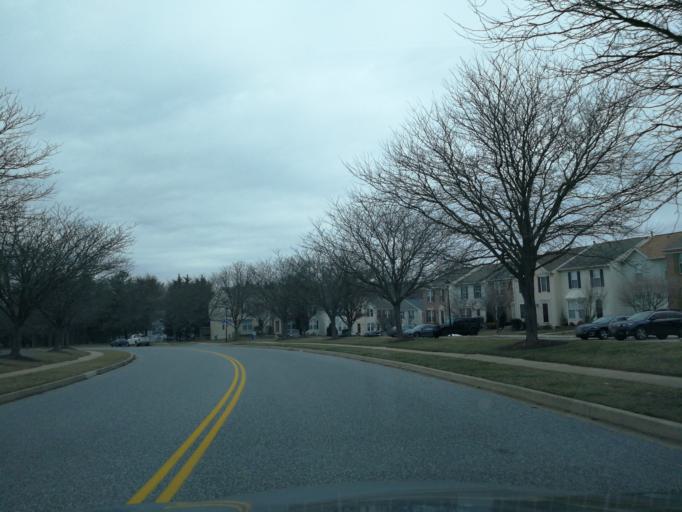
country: US
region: Maryland
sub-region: Harford County
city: Bel Air South
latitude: 39.4747
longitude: -76.3202
